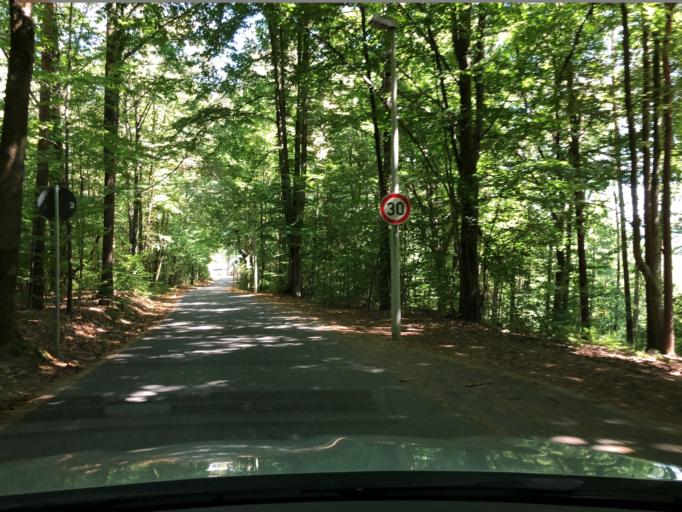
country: DE
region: Bavaria
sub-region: Regierungsbezirk Mittelfranken
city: Ruckersdorf
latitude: 49.5054
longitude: 11.2561
